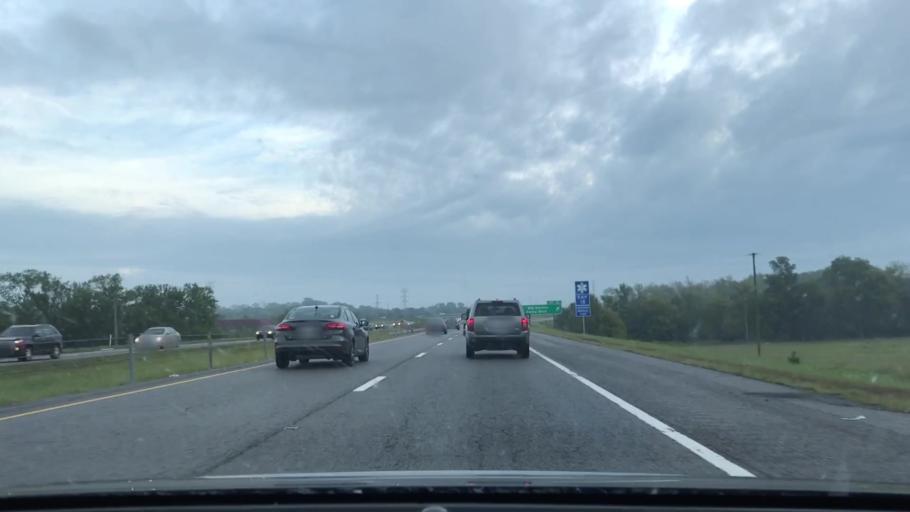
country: US
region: Tennessee
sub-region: Sumner County
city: Shackle Island
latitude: 36.3536
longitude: -86.5393
